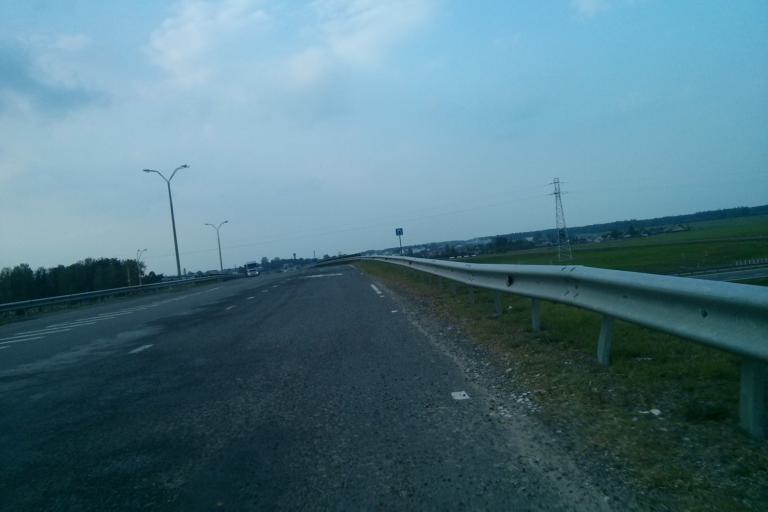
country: BY
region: Minsk
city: Chervyen'
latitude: 53.7231
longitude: 28.3948
